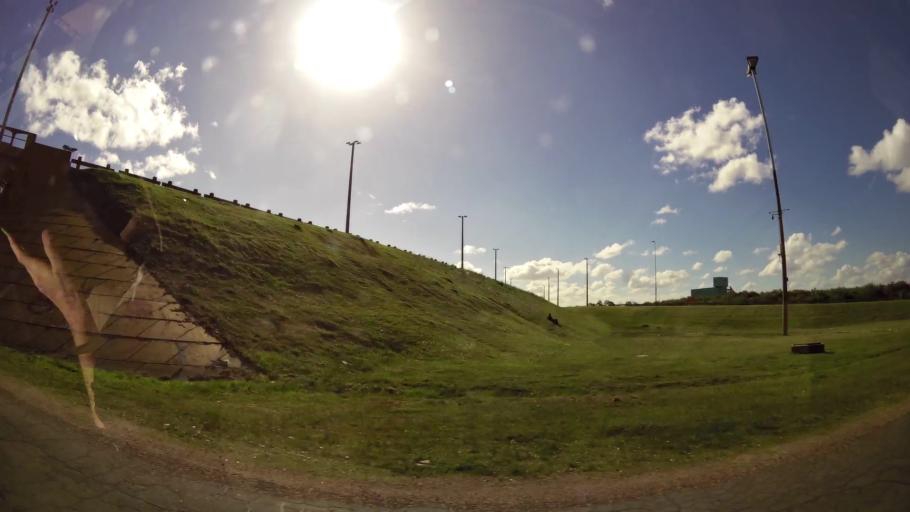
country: UY
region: Montevideo
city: Montevideo
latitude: -34.8569
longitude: -56.2565
